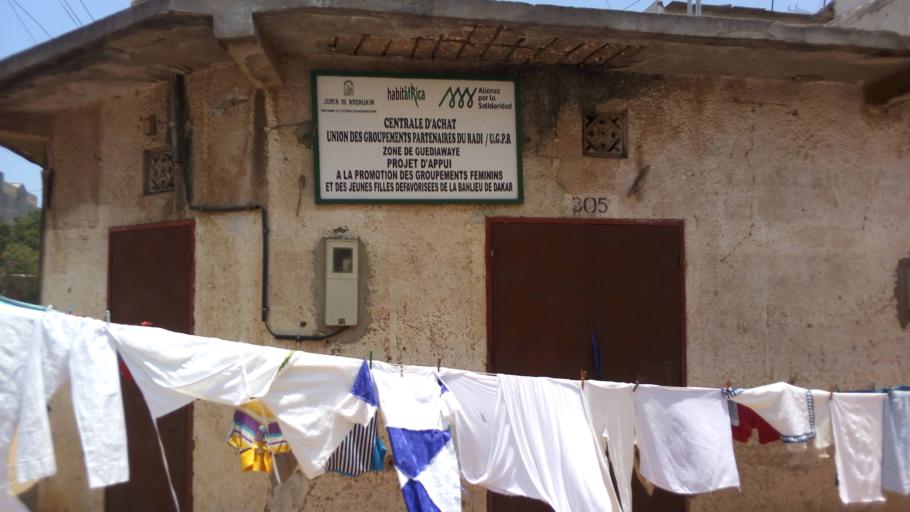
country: SN
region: Dakar
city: Pikine
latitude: 14.7793
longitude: -17.3762
